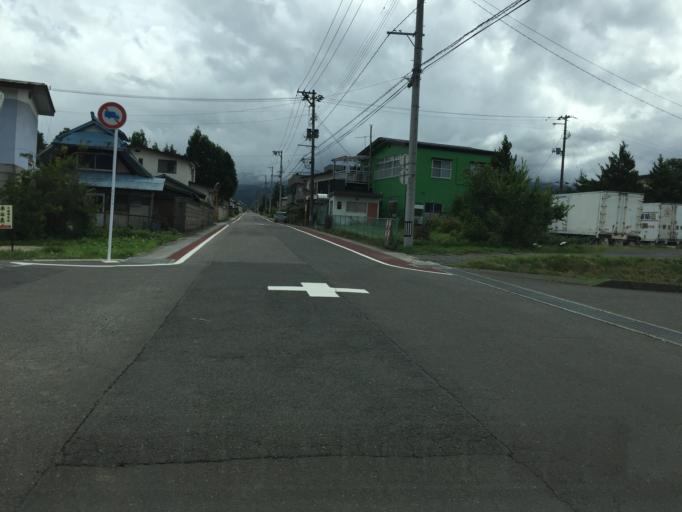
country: JP
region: Fukushima
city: Fukushima-shi
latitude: 37.7274
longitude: 140.3979
